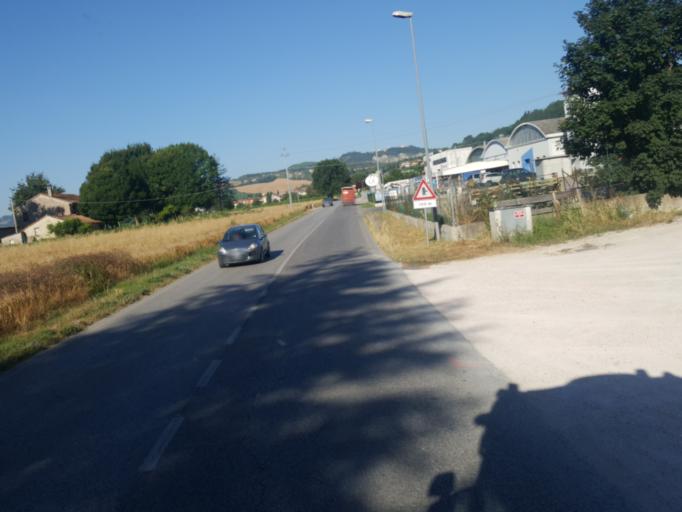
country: IT
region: The Marches
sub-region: Provincia di Pesaro e Urbino
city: Borgo Massano
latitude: 43.8231
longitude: 12.6796
